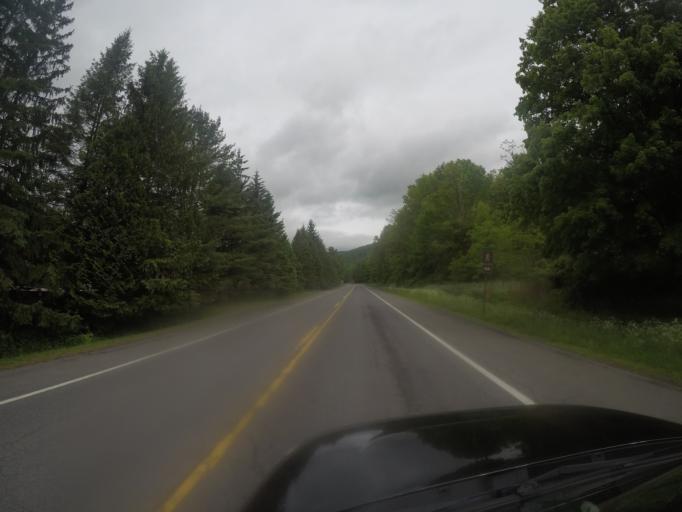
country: US
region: New York
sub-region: Ulster County
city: Shokan
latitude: 42.1085
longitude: -74.3533
